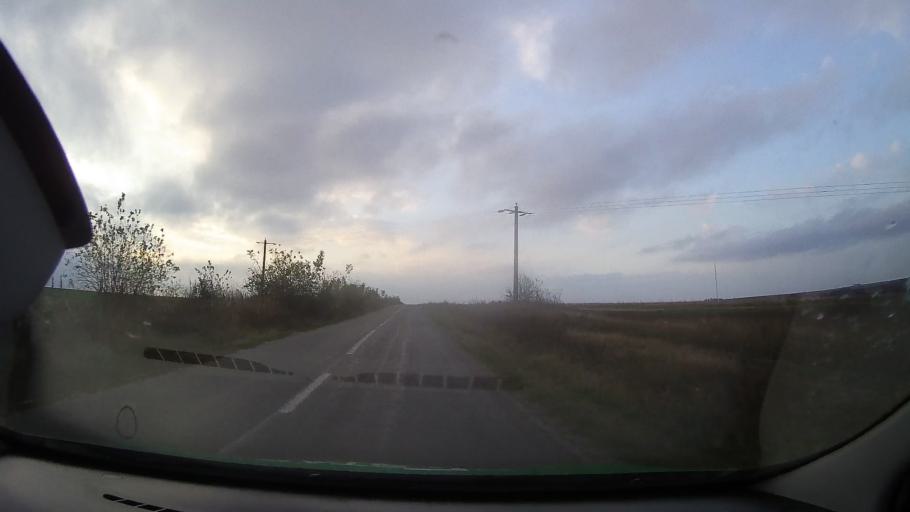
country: RO
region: Constanta
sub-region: Comuna Dobromir
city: Dobromir
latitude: 44.0337
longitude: 27.7661
